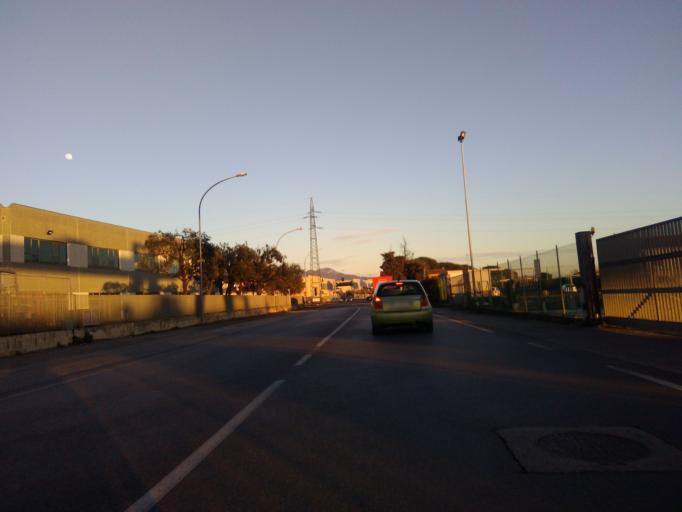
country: IT
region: Tuscany
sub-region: Provincia di Massa-Carrara
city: Carrara
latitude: 44.0337
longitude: 10.0848
